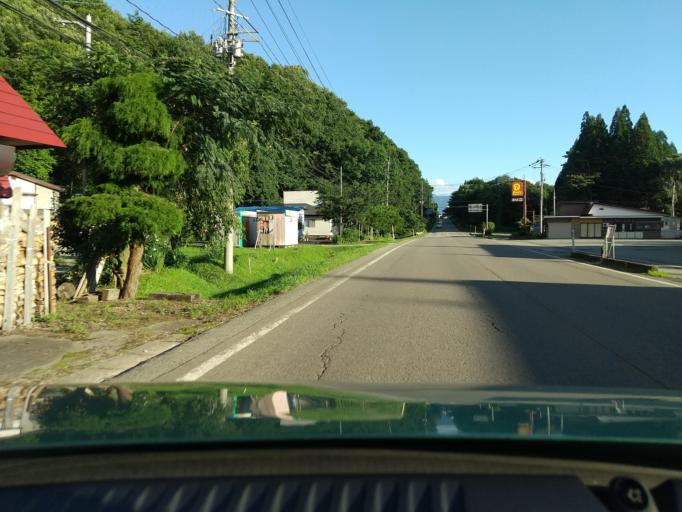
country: JP
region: Akita
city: Kakunodatemachi
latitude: 39.7372
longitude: 140.7177
